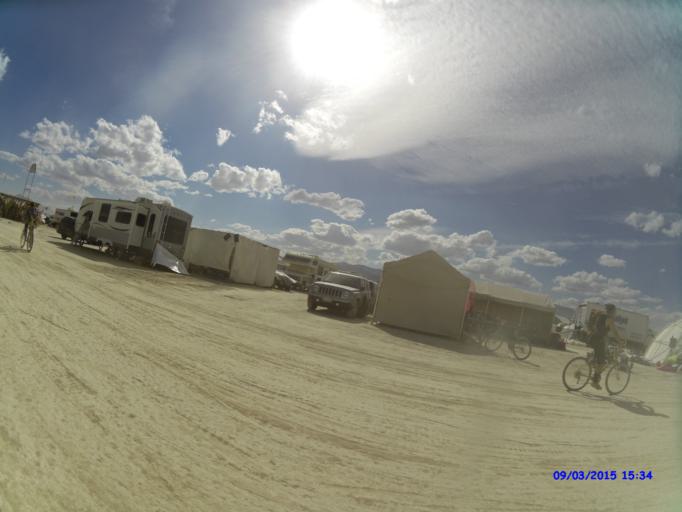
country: US
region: Nevada
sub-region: Pershing County
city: Lovelock
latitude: 40.7854
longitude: -119.2179
